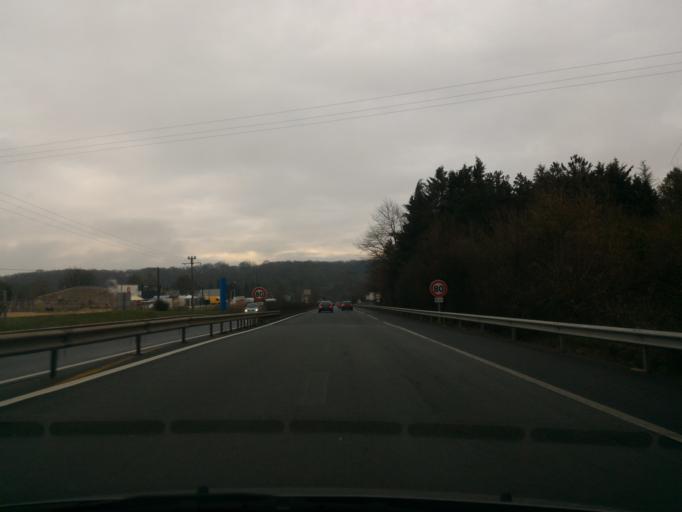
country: FR
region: Poitou-Charentes
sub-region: Departement de la Vienne
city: Fontaine-le-Comte
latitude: 46.5312
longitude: 0.2830
